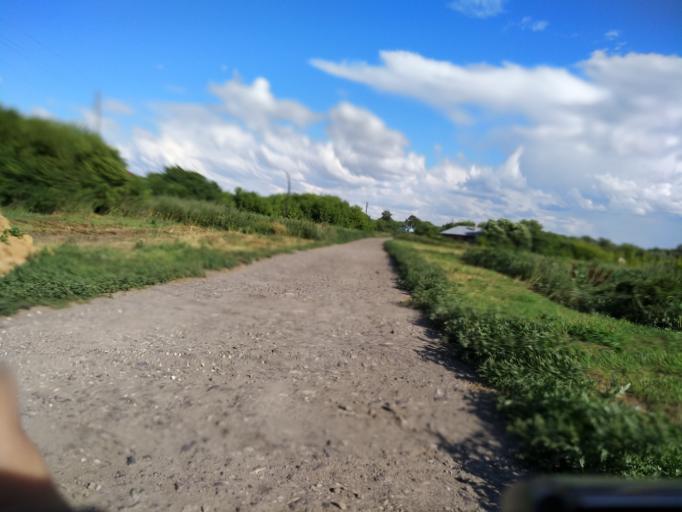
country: RU
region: Lipetsk
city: Dobrinka
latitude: 52.0338
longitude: 40.5613
